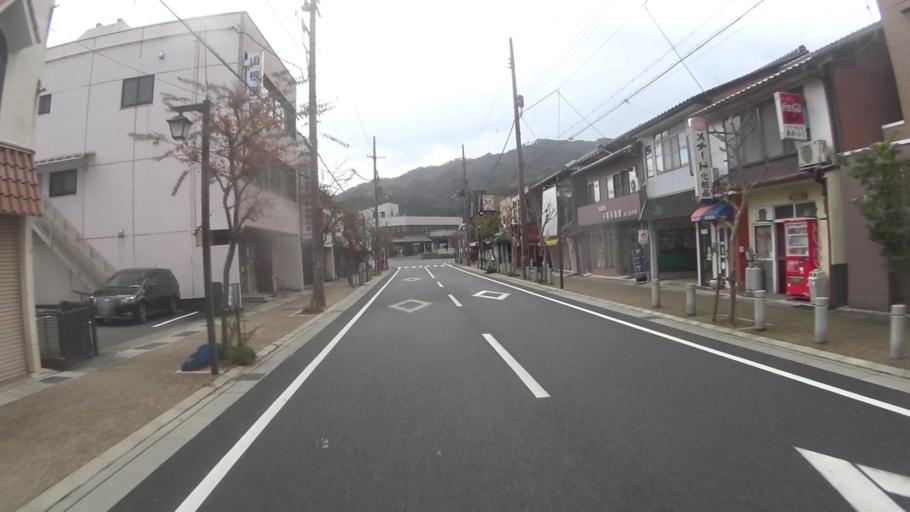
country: JP
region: Kyoto
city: Miyazu
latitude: 35.5351
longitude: 135.1984
